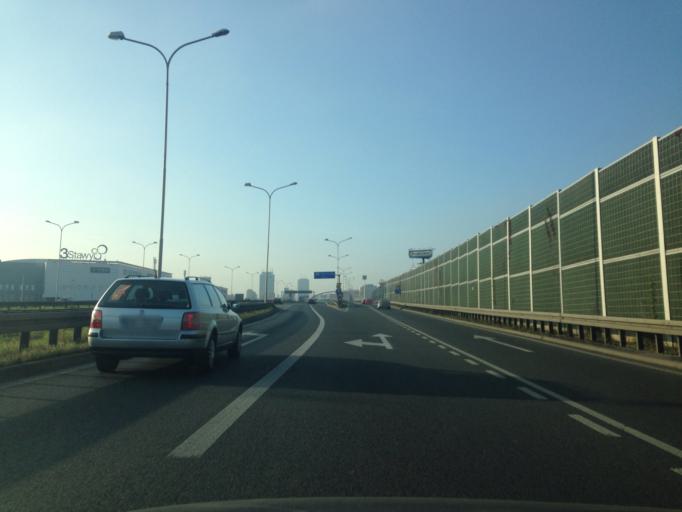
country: PL
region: Silesian Voivodeship
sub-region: Katowice
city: Katowice
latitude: 50.2438
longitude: 19.0427
